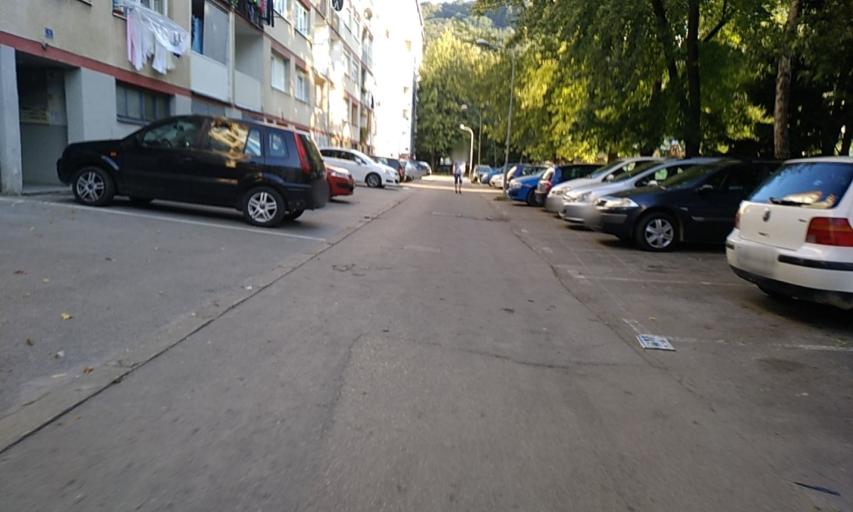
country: BA
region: Republika Srpska
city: Mejdan - Obilicevo
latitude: 44.7602
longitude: 17.1946
